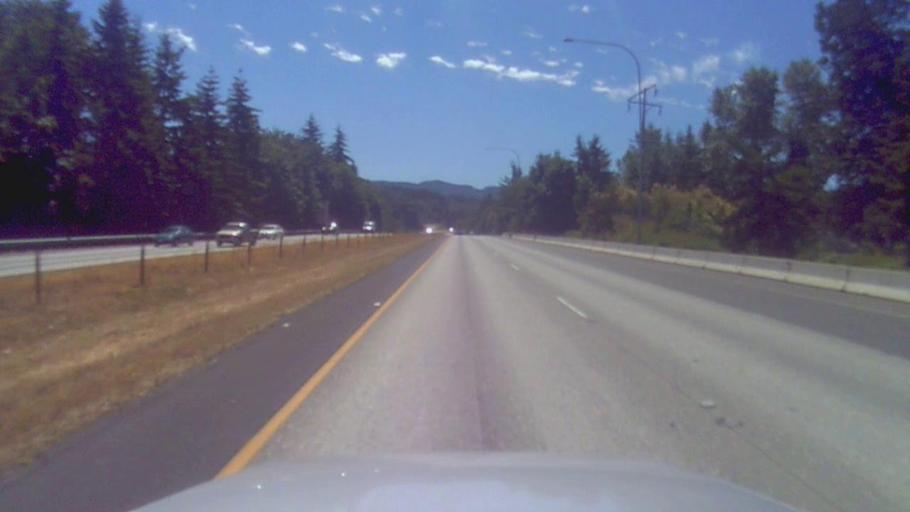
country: US
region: Washington
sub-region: Whatcom County
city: Bellingham
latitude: 48.7402
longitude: -122.4677
